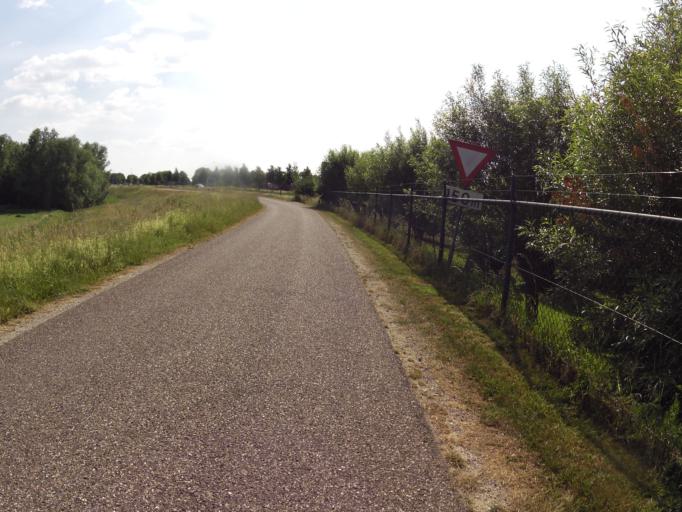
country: NL
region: Gelderland
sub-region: Gemeente Neerijnen
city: Neerijnen
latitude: 51.7941
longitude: 5.3237
